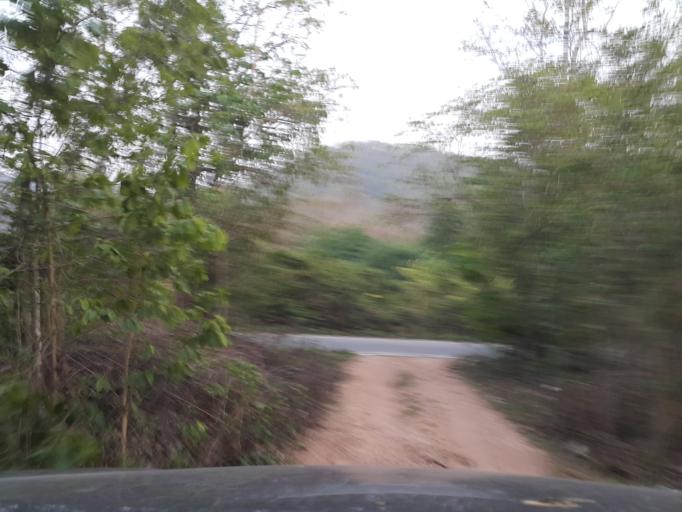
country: TH
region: Lamphun
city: Thung Hua Chang
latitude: 17.8937
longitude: 99.0860
